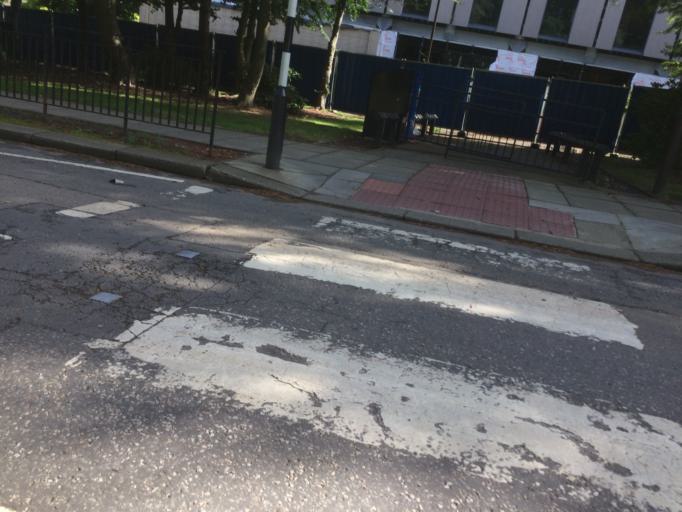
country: GB
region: Scotland
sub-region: Edinburgh
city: Currie
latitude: 55.9111
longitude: -3.3168
